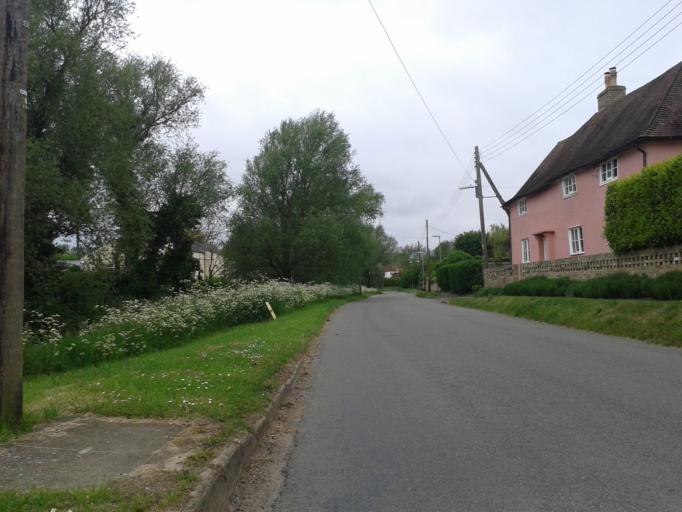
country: GB
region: England
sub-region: Cambridgeshire
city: Sawtry
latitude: 52.3779
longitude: -0.2709
